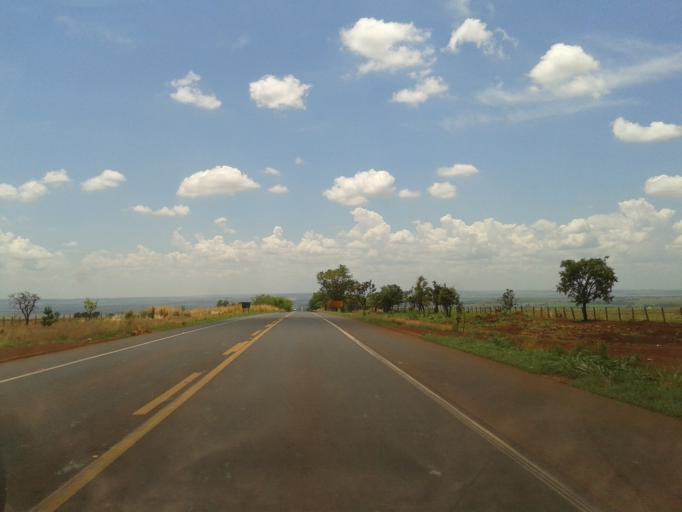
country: BR
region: Goias
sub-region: Goiatuba
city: Goiatuba
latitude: -18.2530
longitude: -49.6828
